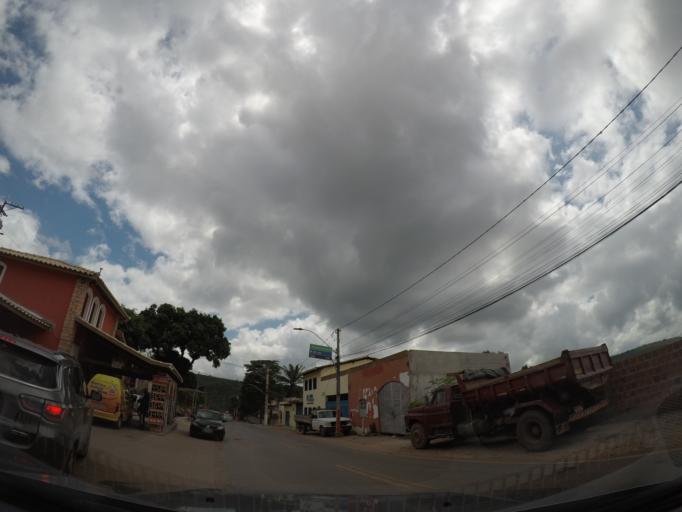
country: BR
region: Bahia
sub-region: Andarai
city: Vera Cruz
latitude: -12.5606
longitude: -41.3864
